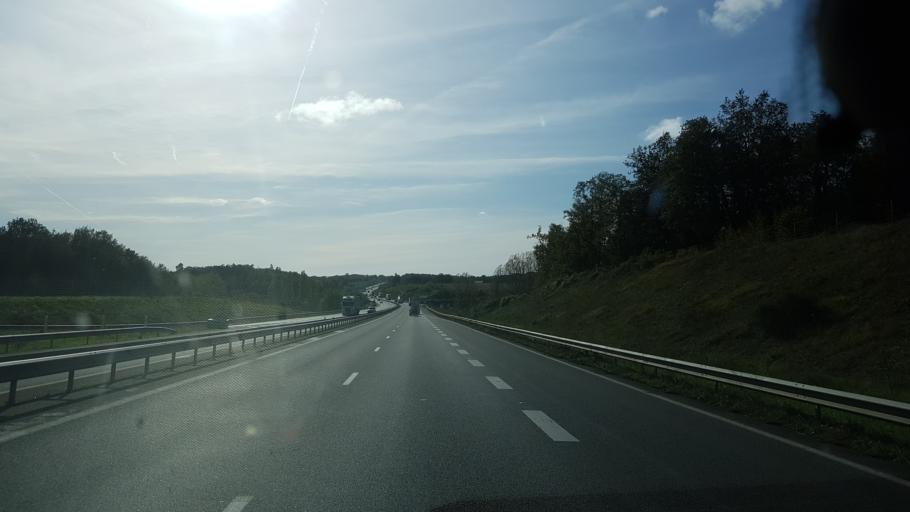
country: FR
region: Poitou-Charentes
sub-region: Departement de la Charente
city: Saint-Projet-Saint-Constant
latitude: 45.7371
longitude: 0.3431
